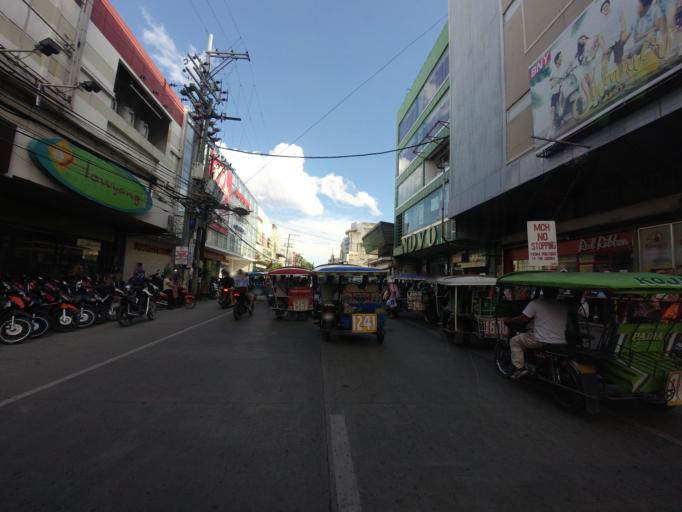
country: PH
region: Central Visayas
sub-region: Province of Negros Oriental
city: Dumaguete
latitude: 9.3078
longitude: 123.3076
